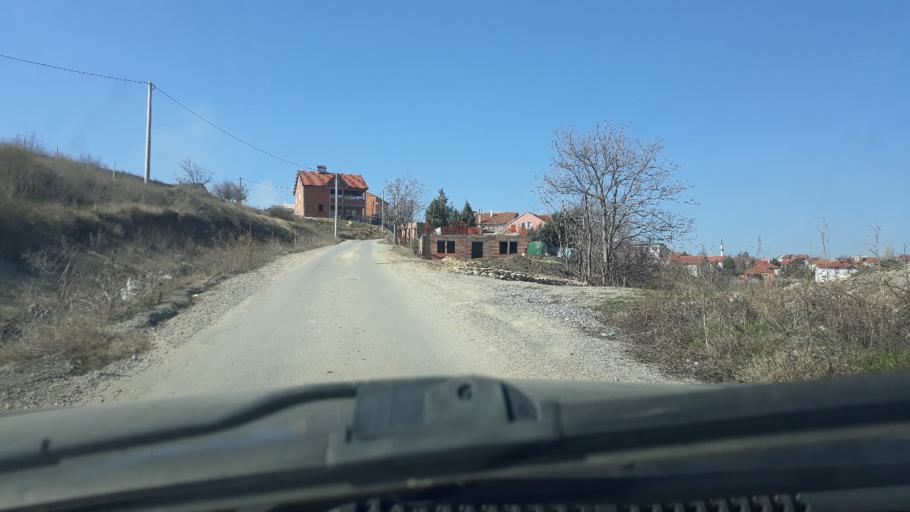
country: MK
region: Veles
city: Gorno Orizari
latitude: 41.6809
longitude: 21.7356
